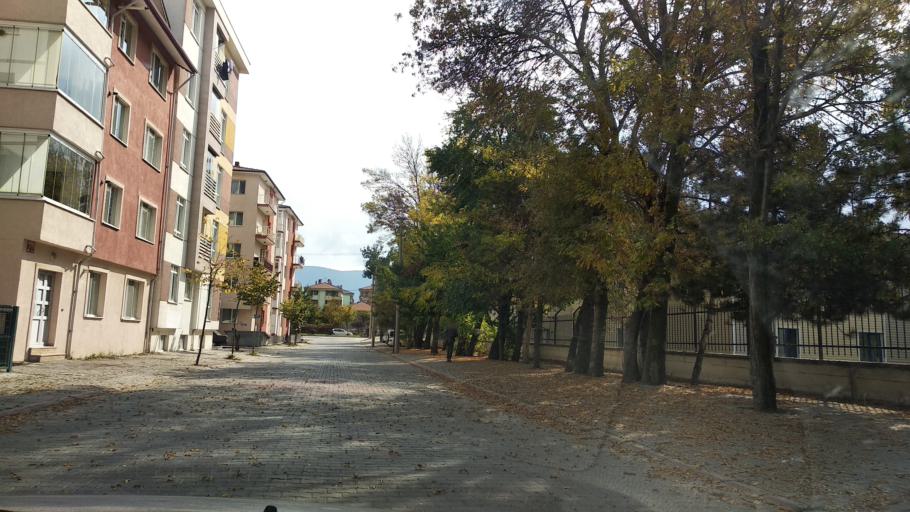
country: TR
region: Bolu
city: Bolu
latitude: 40.7395
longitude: 31.6042
